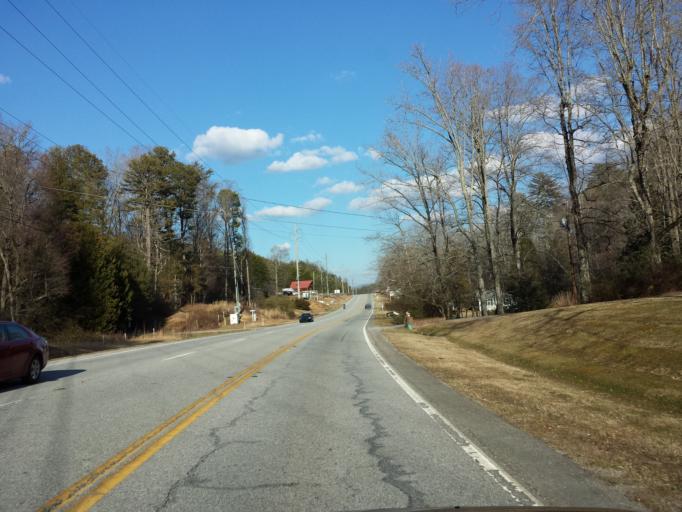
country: US
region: Georgia
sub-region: White County
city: Cleveland
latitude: 34.6580
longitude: -83.7285
